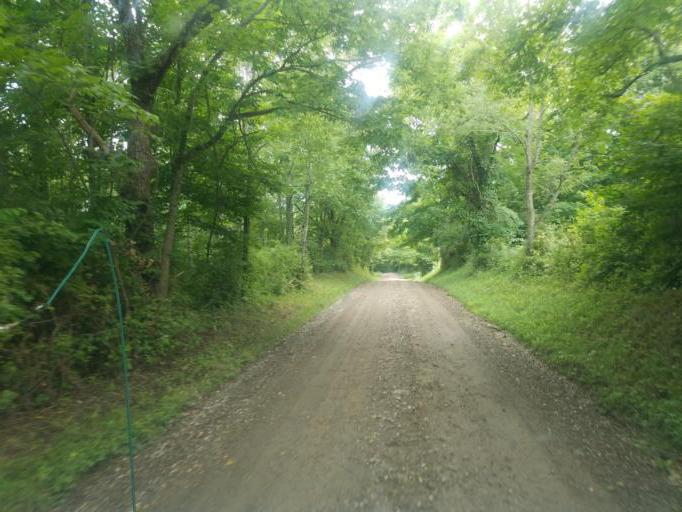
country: US
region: Ohio
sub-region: Knox County
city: Oak Hill
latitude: 40.3285
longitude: -82.1294
